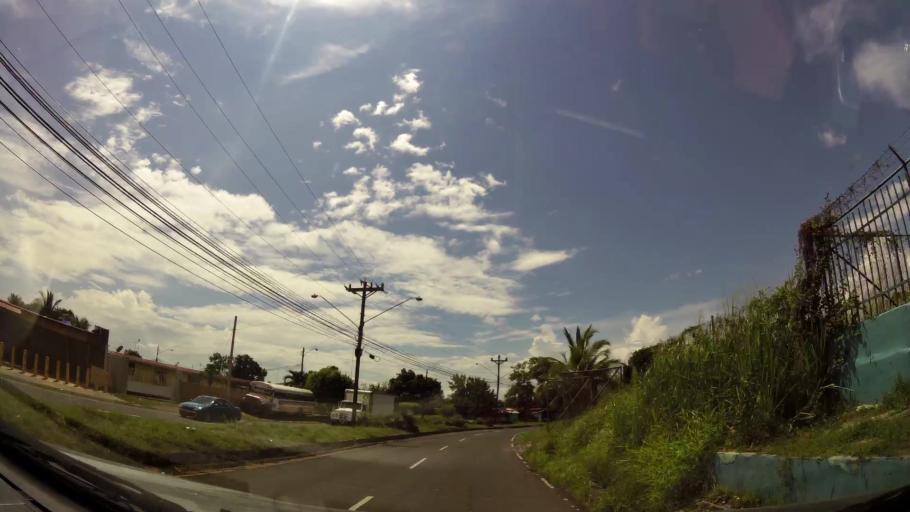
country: PA
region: Panama
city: Nuevo Arraijan
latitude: 8.9152
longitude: -79.7000
